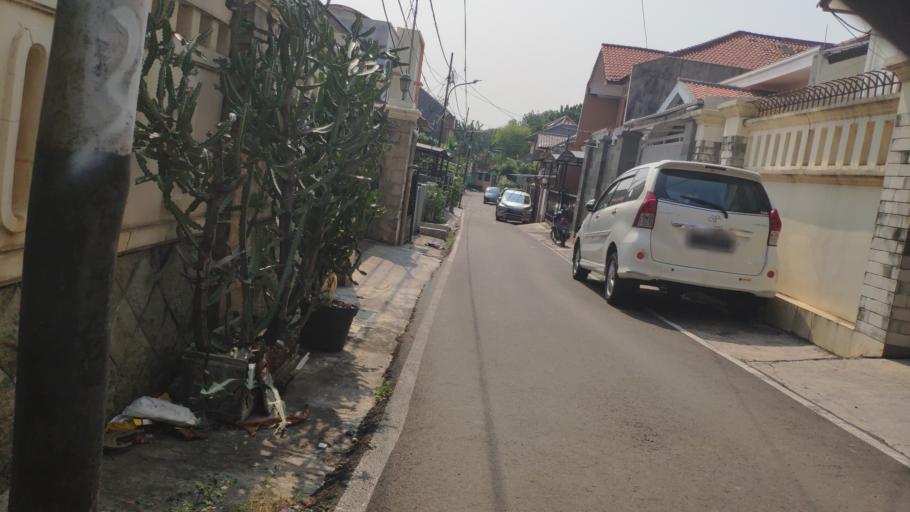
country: ID
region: Jakarta Raya
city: Jakarta
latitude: -6.2502
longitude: 106.7972
